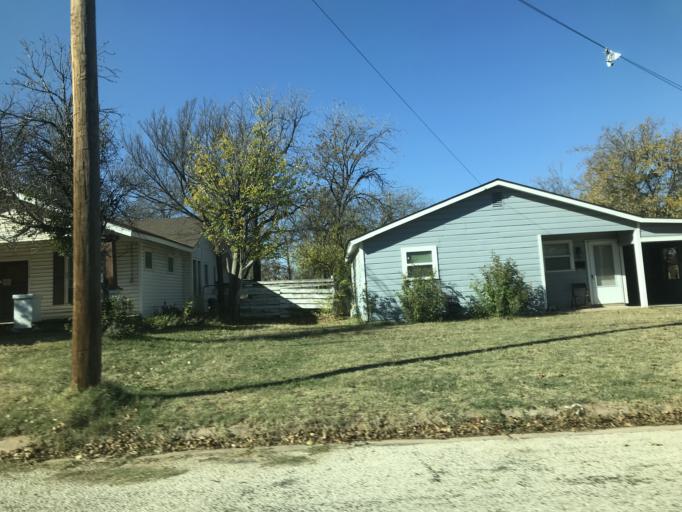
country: US
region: Texas
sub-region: Taylor County
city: Abilene
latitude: 32.4565
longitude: -99.7489
